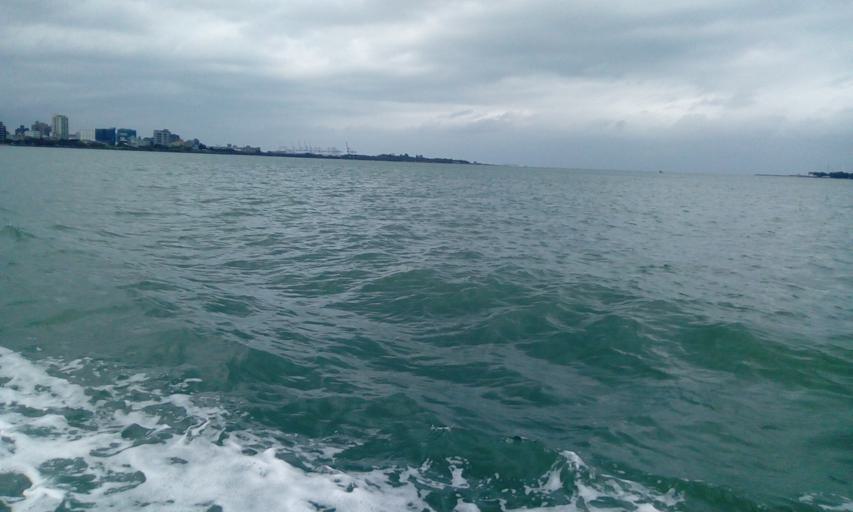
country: TW
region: Taipei
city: Taipei
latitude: 25.1667
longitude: 121.4377
